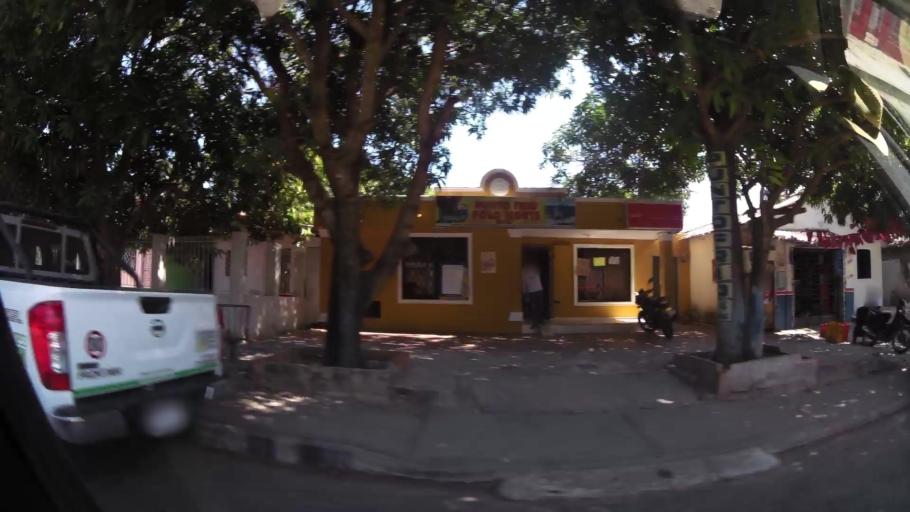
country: CO
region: Atlantico
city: Barranquilla
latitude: 10.9781
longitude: -74.8257
